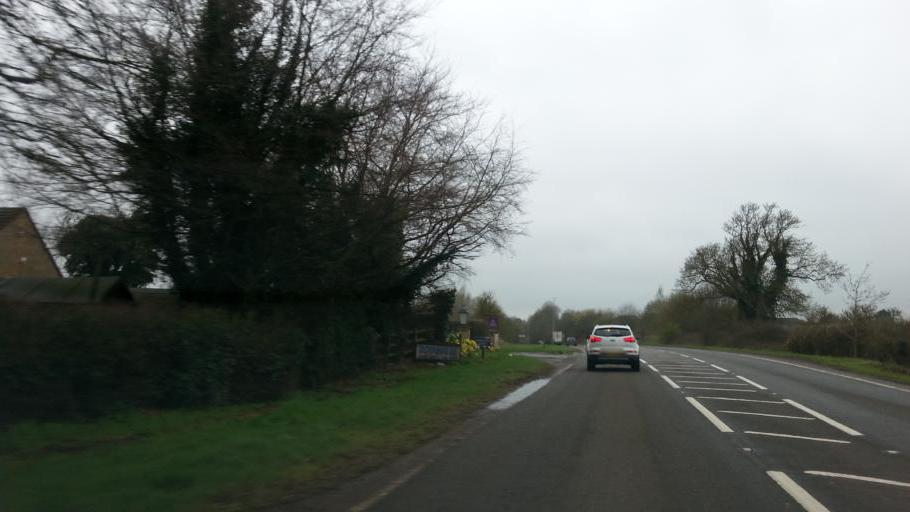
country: GB
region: England
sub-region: Oxfordshire
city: Adderbury
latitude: 52.0672
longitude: -1.2577
